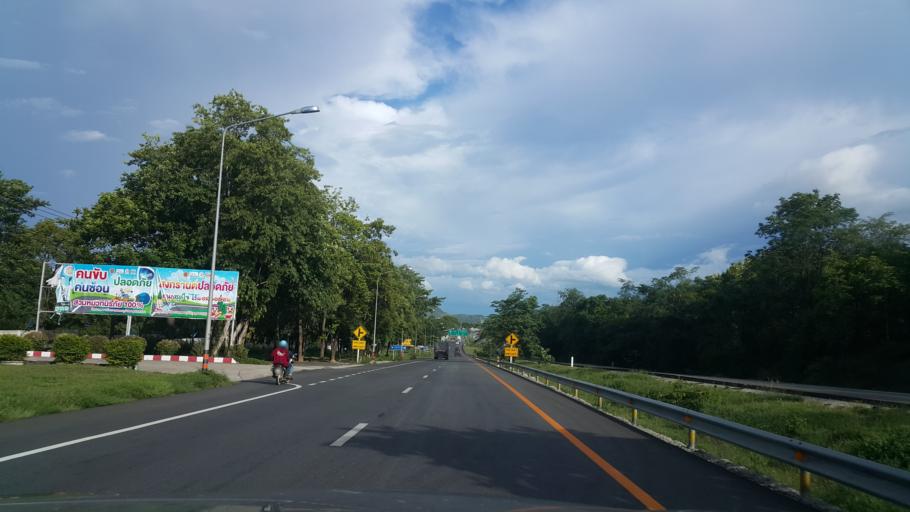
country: TH
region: Tak
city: Ban Tak
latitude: 17.0397
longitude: 99.0846
